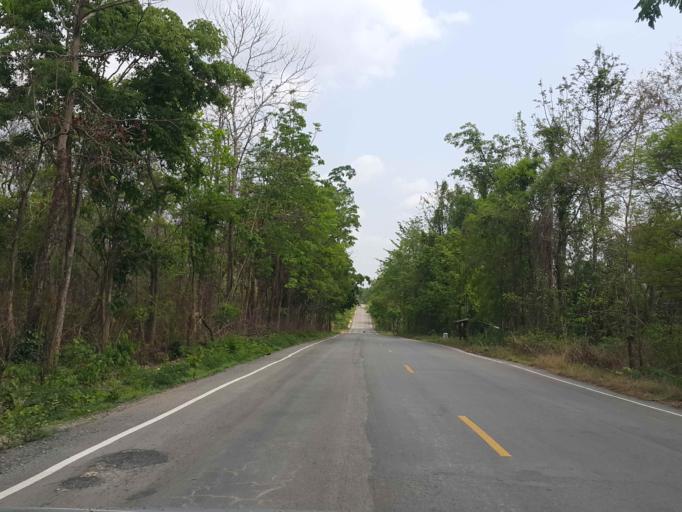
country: TH
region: Sukhothai
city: Thung Saliam
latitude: 17.3930
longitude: 99.3944
